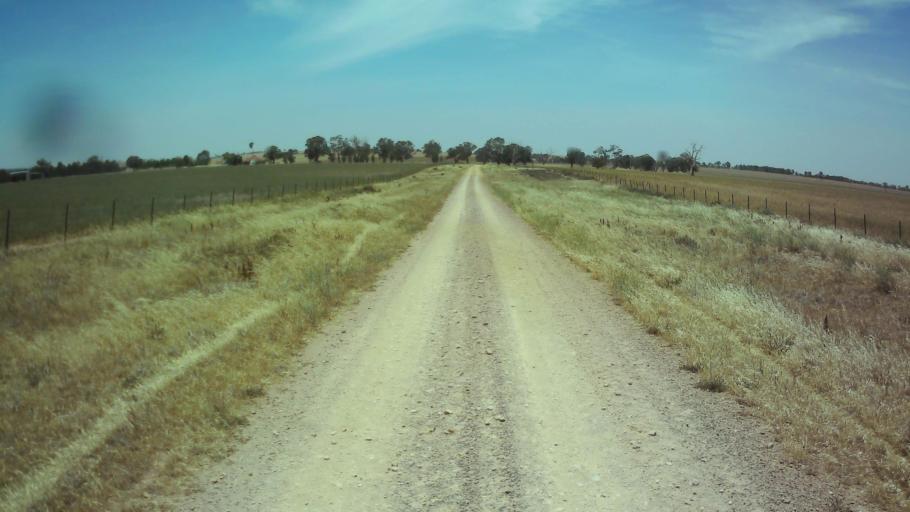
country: AU
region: New South Wales
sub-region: Weddin
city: Grenfell
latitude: -34.0008
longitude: 148.3980
